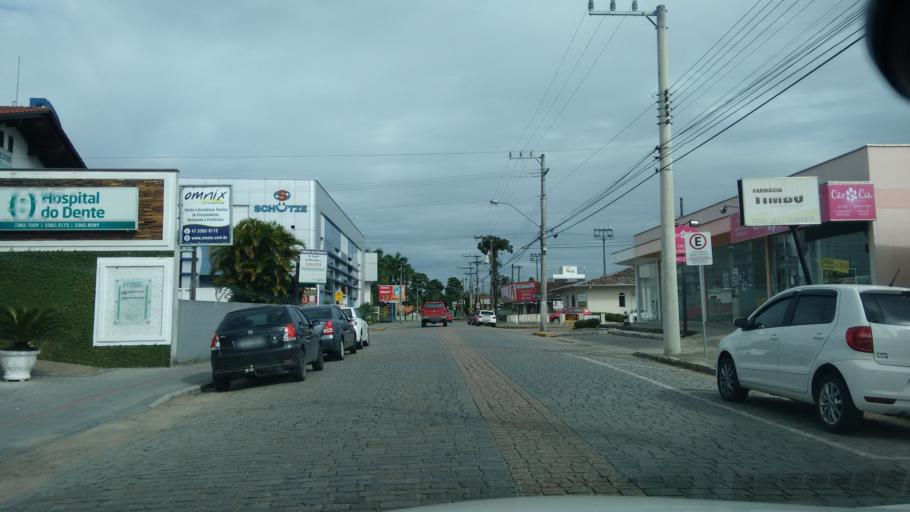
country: BR
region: Santa Catarina
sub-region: Timbo
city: Timbo
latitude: -26.8269
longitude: -49.2719
